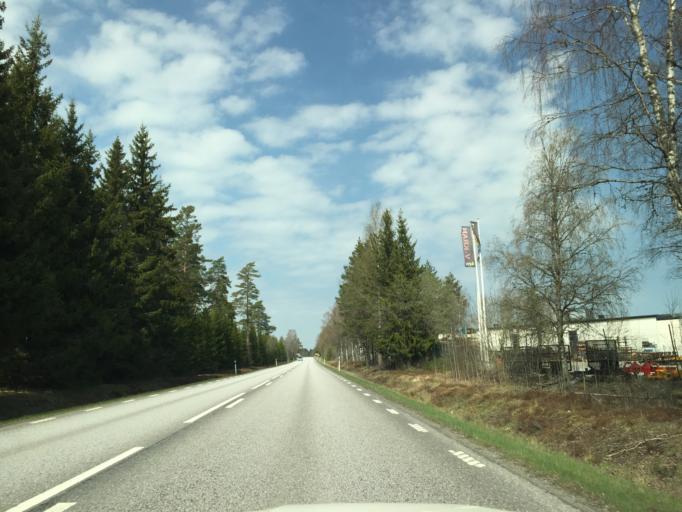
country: SE
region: Vaestra Goetaland
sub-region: Bengtsfors Kommun
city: Dals Langed
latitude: 58.8073
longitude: 12.1487
